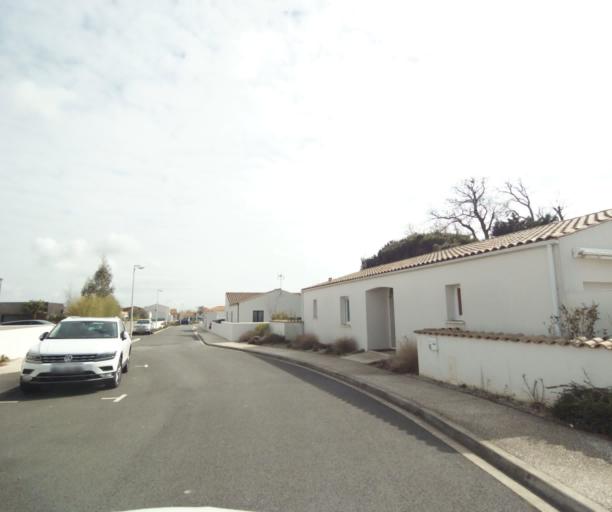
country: FR
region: Poitou-Charentes
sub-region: Departement de la Charente-Maritime
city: Lagord
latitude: 46.1807
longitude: -1.1613
